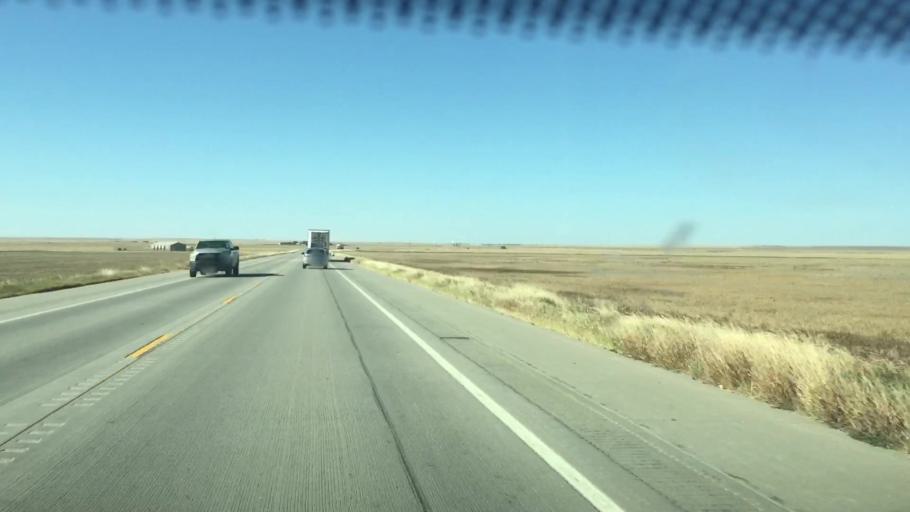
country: US
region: Colorado
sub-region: Kiowa County
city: Eads
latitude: 38.3684
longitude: -102.7256
